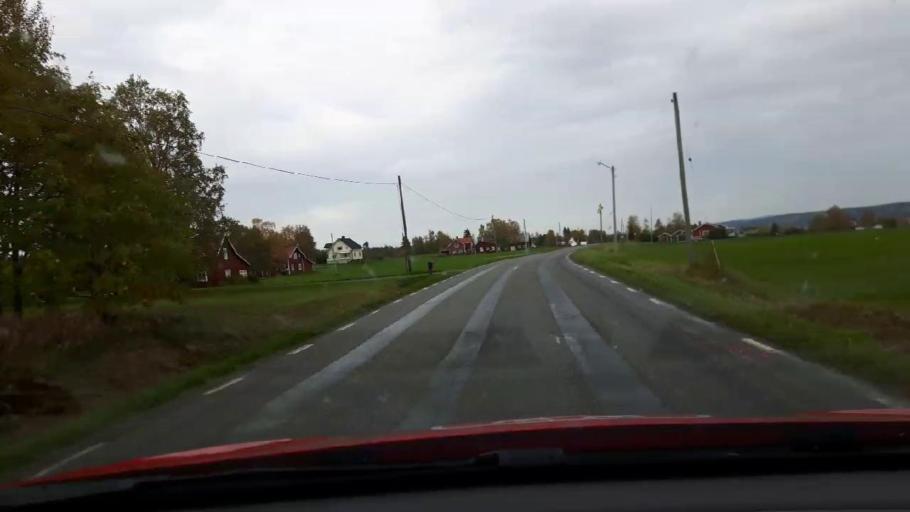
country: SE
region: Jaemtland
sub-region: Bergs Kommun
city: Hoverberg
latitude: 62.8509
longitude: 14.3822
